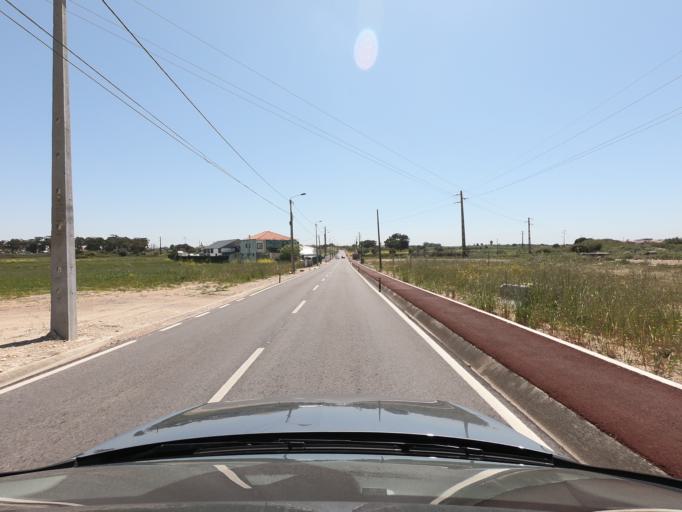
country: PT
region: Lisbon
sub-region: Cascais
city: Parede
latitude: 38.7356
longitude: -9.3541
